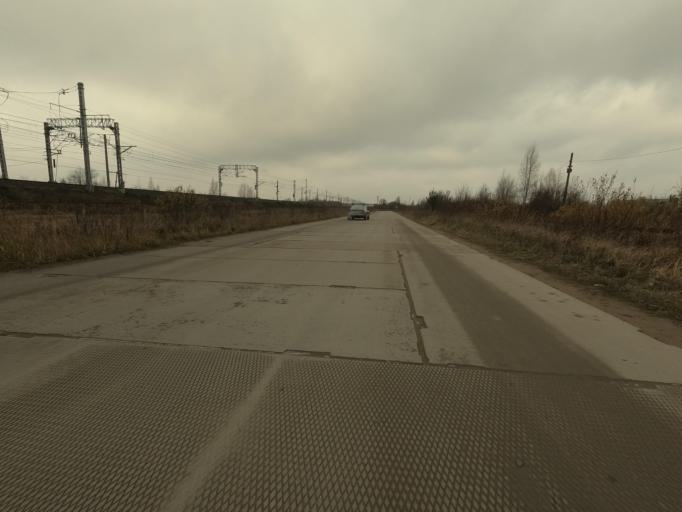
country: RU
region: Leningrad
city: Lyuban'
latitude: 59.4770
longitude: 31.2573
